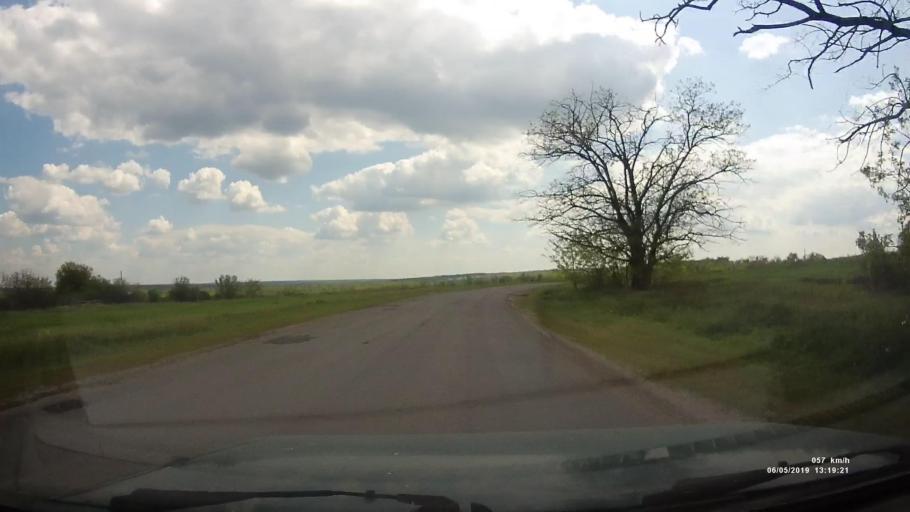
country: RU
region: Rostov
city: Ust'-Donetskiy
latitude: 47.7262
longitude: 40.9141
